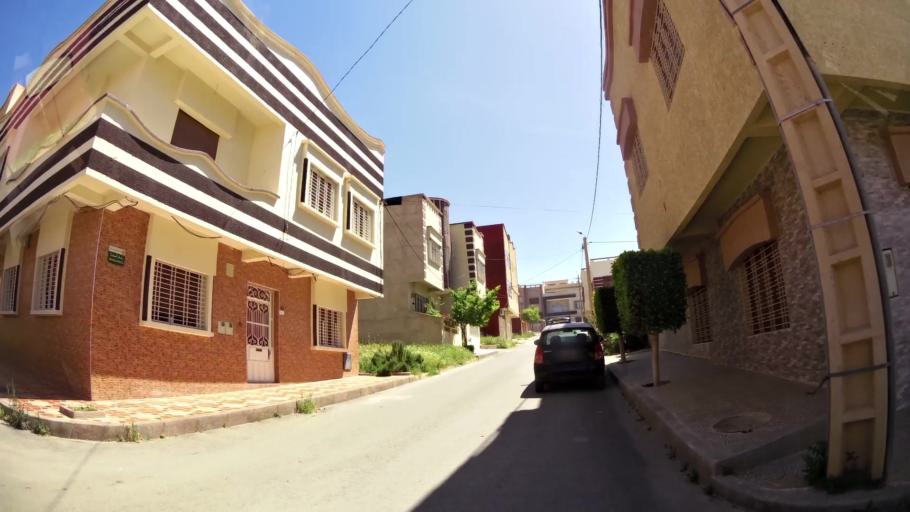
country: MA
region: Oriental
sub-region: Oujda-Angad
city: Oujda
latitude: 34.6482
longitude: -1.9101
